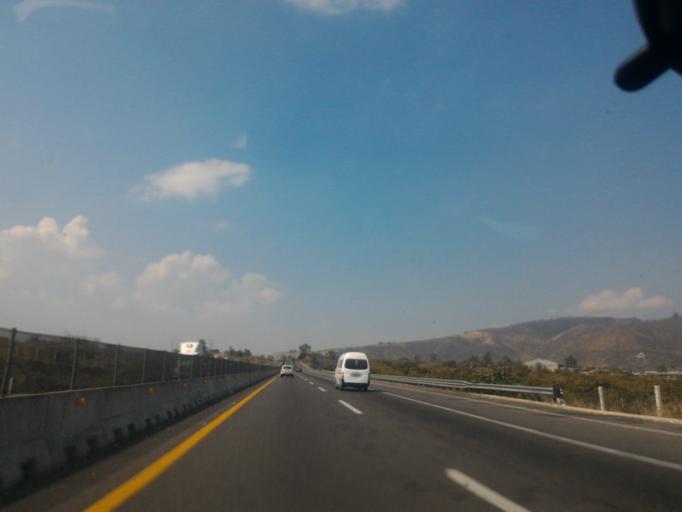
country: MX
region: Jalisco
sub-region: Zapotlan el Grande
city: Ciudad Guzman [CERESO]
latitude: 19.6324
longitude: -103.4664
